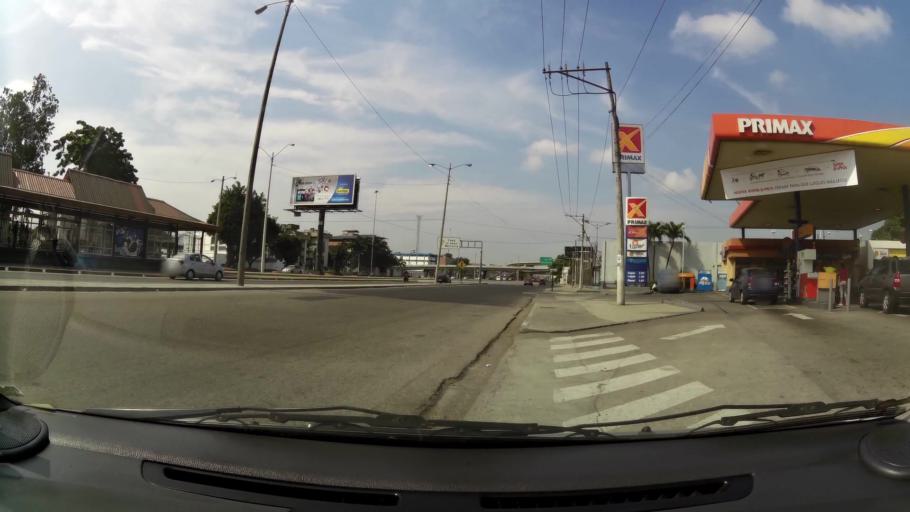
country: EC
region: Guayas
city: Guayaquil
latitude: -2.2367
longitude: -79.8969
